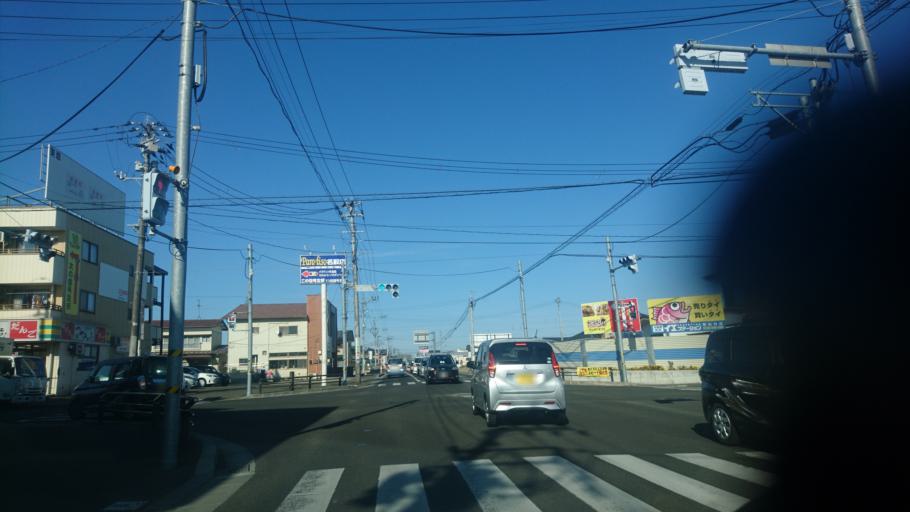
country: JP
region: Miyagi
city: Iwanuma
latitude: 38.1796
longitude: 140.8857
